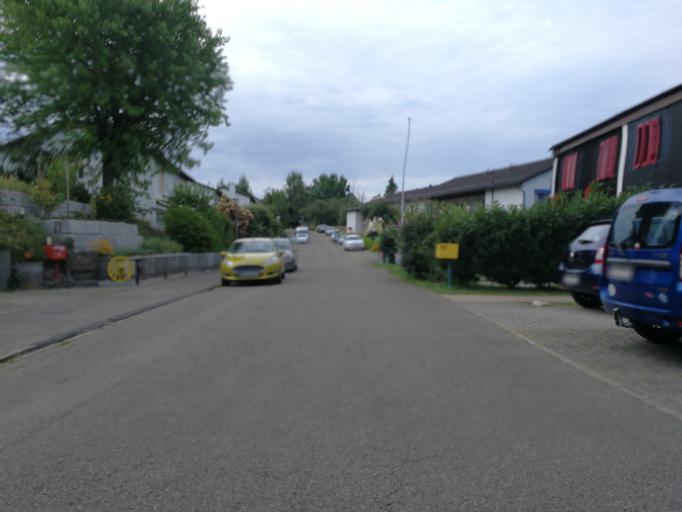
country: CH
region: Zurich
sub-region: Bezirk Hinwil
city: Wetzikon / Robenhausen
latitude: 47.3335
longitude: 8.7614
